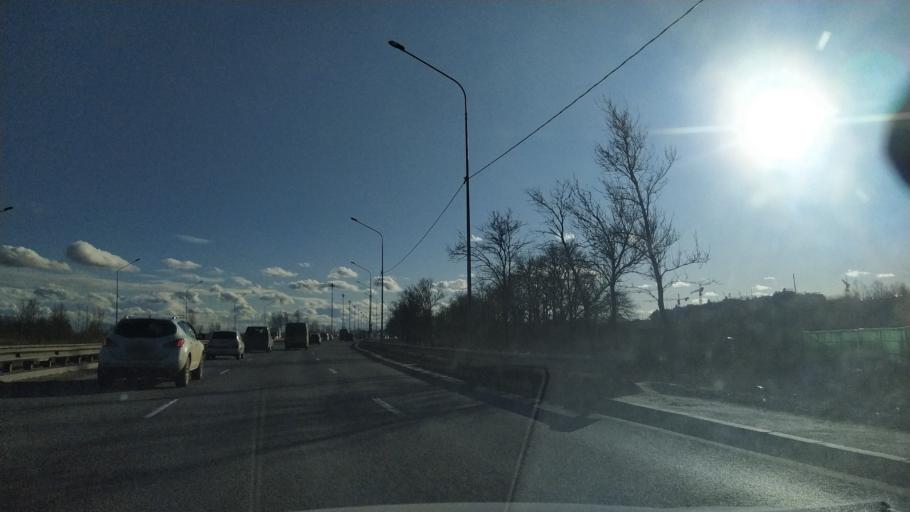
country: RU
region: St.-Petersburg
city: Aleksandrovskaya
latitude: 59.7637
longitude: 30.3293
